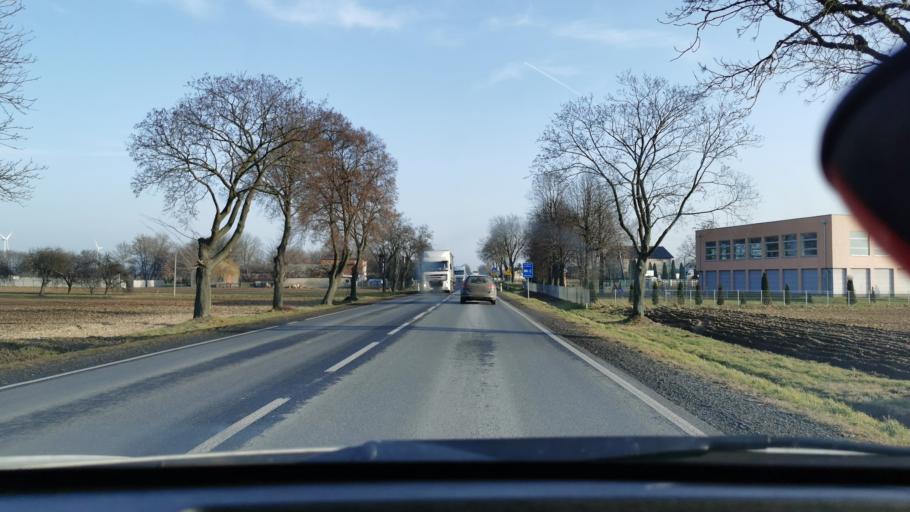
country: PL
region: Lodz Voivodeship
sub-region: Powiat sieradzki
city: Wroblew
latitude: 51.6322
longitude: 18.5443
